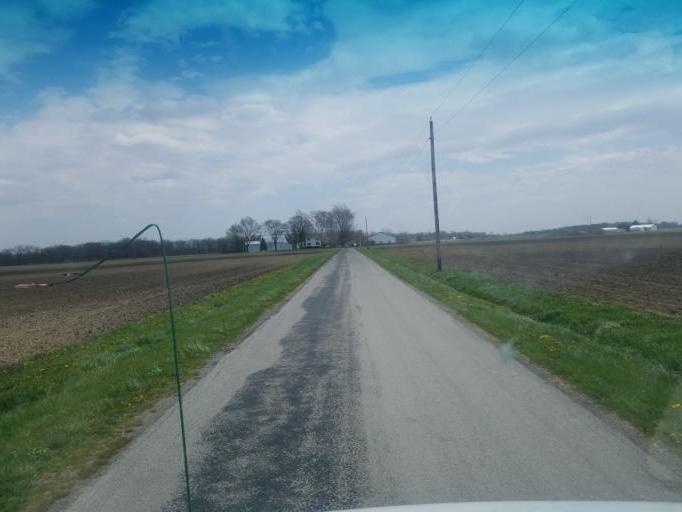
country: US
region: Ohio
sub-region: Wyandot County
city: Upper Sandusky
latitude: 40.7742
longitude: -83.3265
